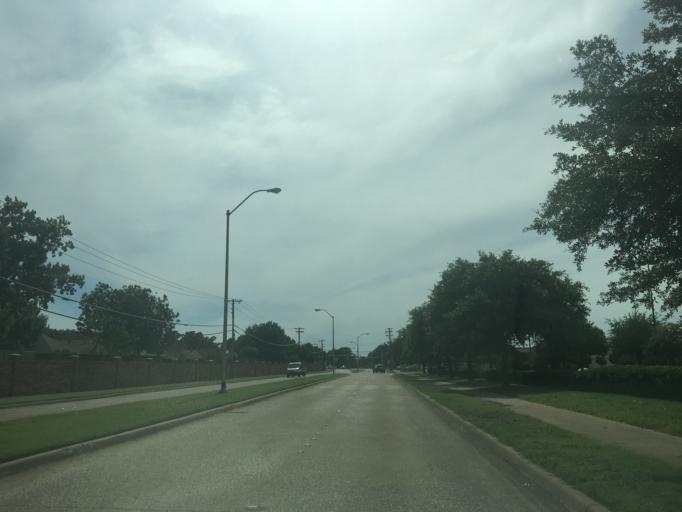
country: US
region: Texas
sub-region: Dallas County
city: Richardson
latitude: 32.9387
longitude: -96.6969
